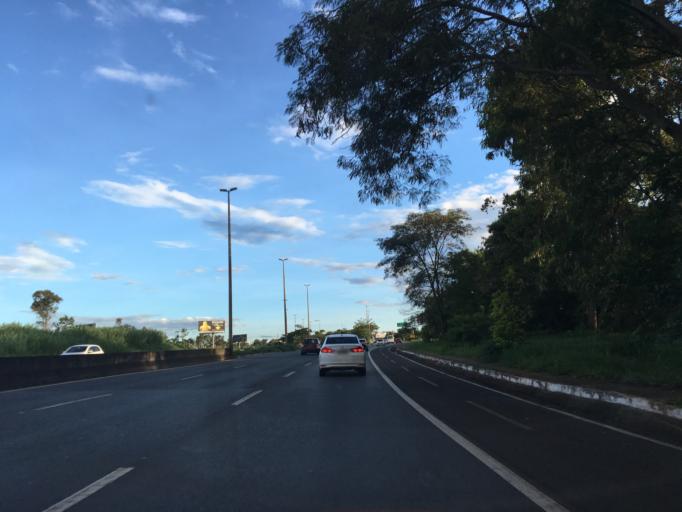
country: BR
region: Federal District
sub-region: Brasilia
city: Brasilia
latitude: -15.8449
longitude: -47.8185
